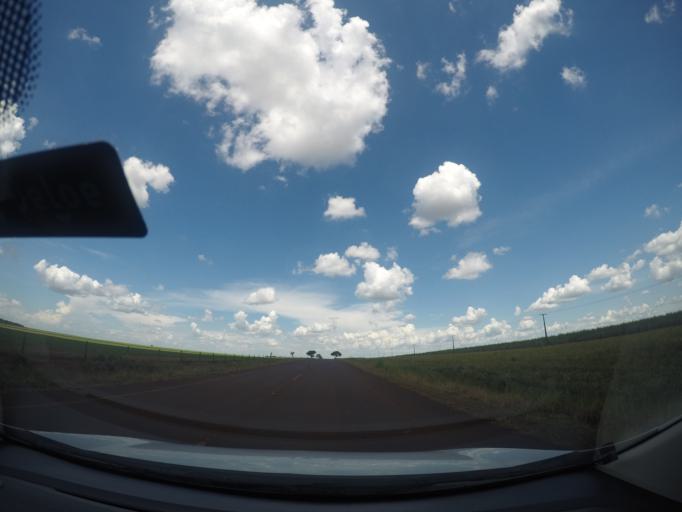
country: BR
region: Minas Gerais
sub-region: Frutal
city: Frutal
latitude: -19.9215
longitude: -48.6767
